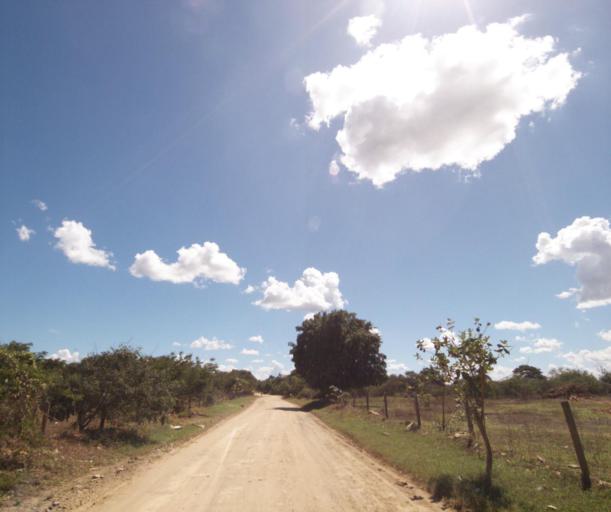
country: BR
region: Bahia
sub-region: Carinhanha
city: Carinhanha
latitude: -14.2230
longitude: -44.2980
